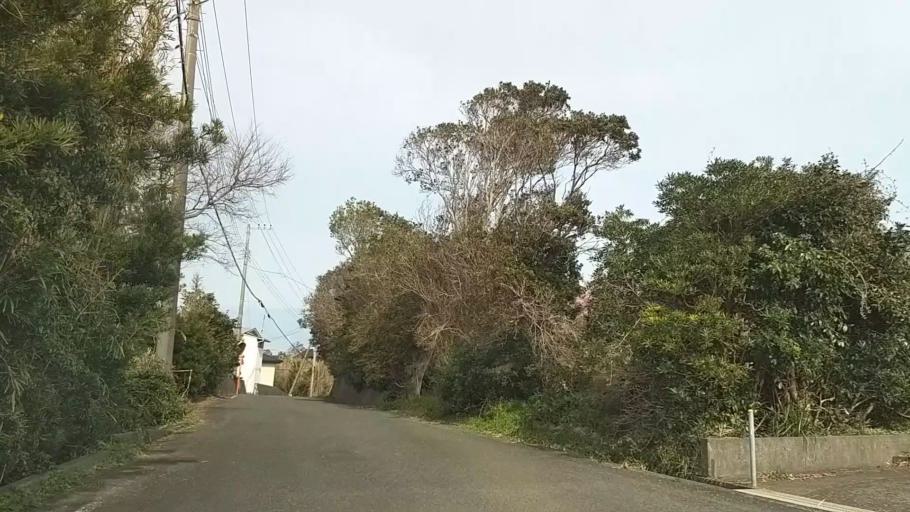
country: JP
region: Shizuoka
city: Shimoda
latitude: 34.6577
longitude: 138.9631
